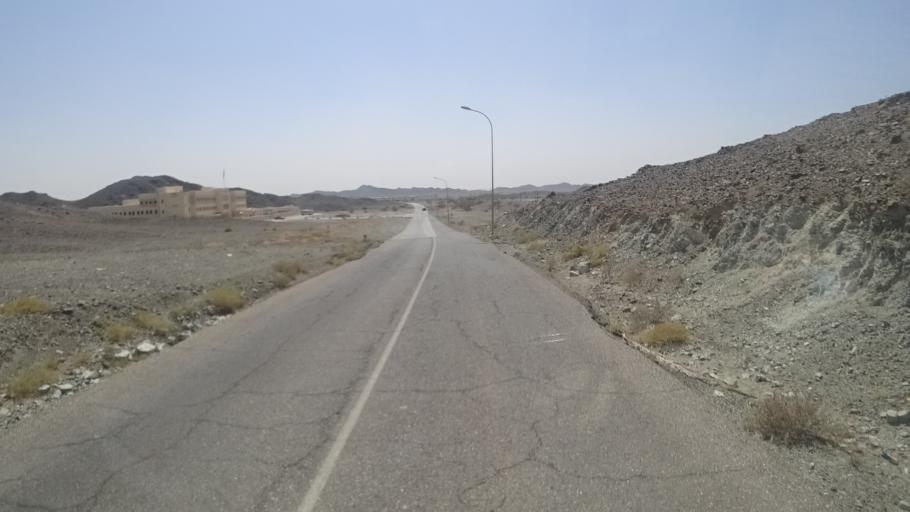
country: OM
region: Ash Sharqiyah
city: Ibra'
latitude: 22.6651
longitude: 58.5291
